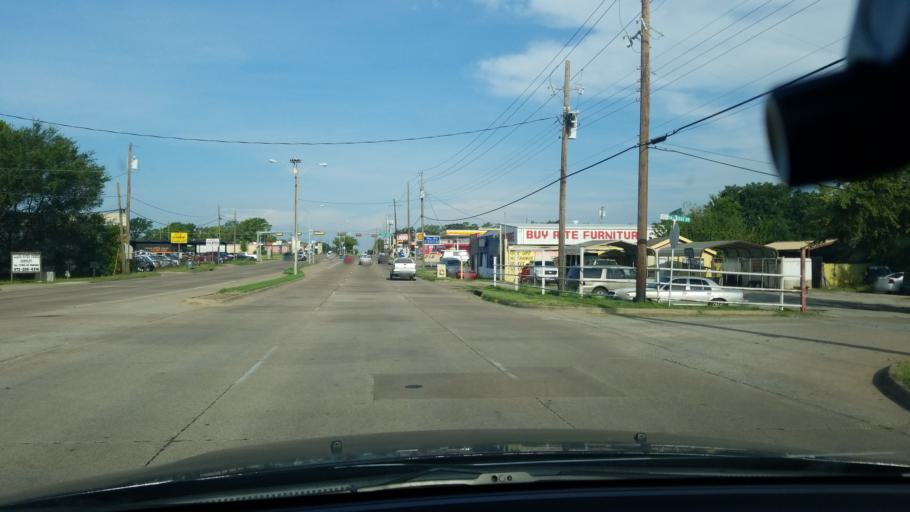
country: US
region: Texas
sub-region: Dallas County
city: Balch Springs
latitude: 32.7342
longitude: -96.6296
